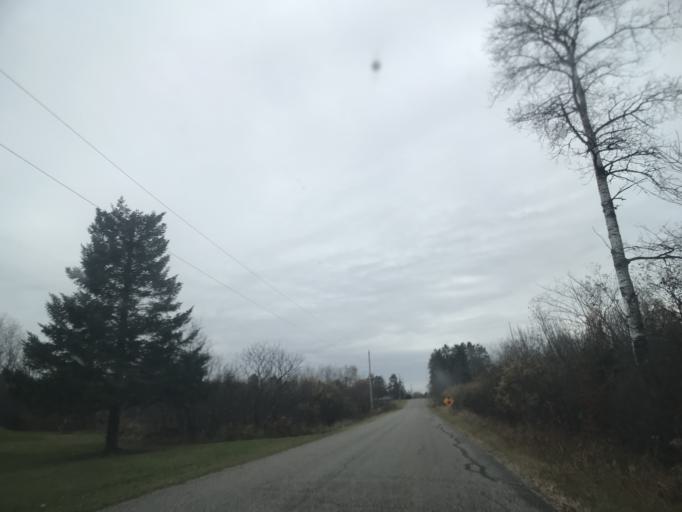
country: US
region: Wisconsin
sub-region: Menominee County
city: Legend Lake
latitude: 45.1814
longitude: -88.4687
